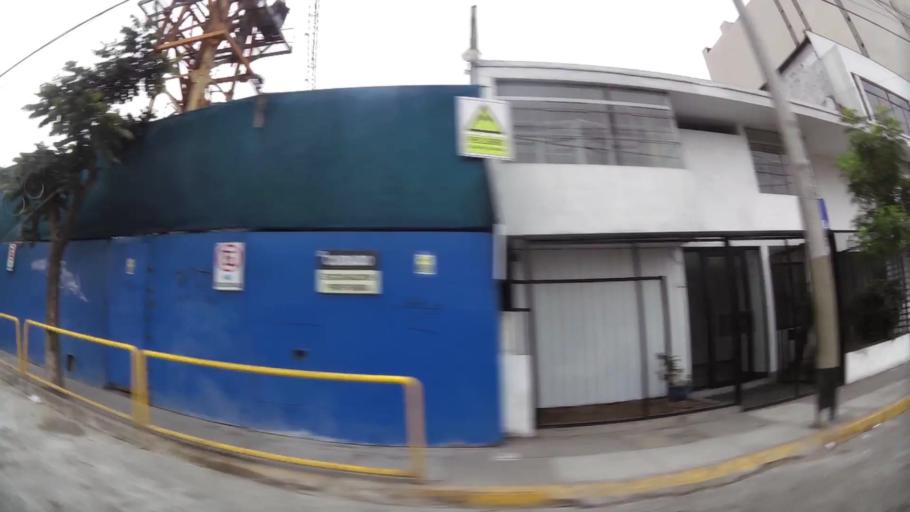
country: PE
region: Lima
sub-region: Lima
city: San Isidro
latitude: -12.1211
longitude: -77.0249
